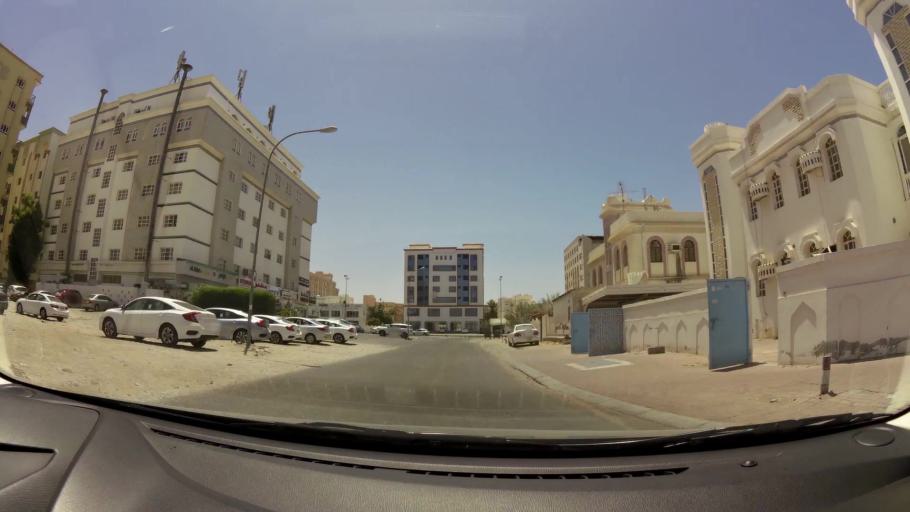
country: OM
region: Muhafazat Masqat
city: Bawshar
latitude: 23.5914
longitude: 58.3851
